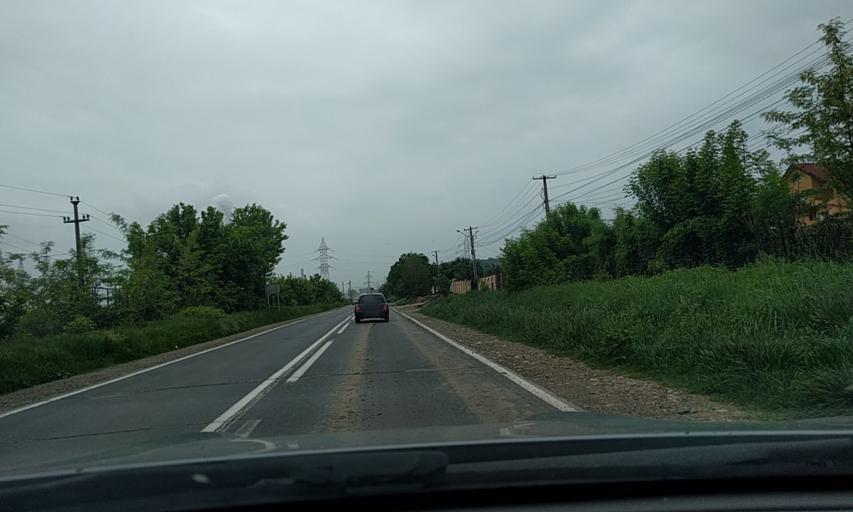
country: RO
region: Dambovita
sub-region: Comuna Aninoasa
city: Sateni
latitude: 44.9806
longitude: 25.4220
